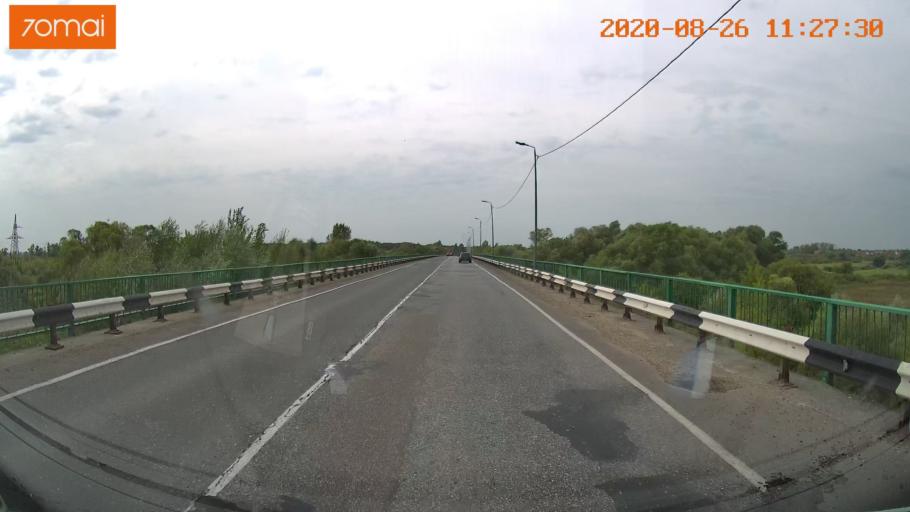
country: RU
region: Rjazan
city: Shilovo
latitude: 54.3254
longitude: 40.9343
